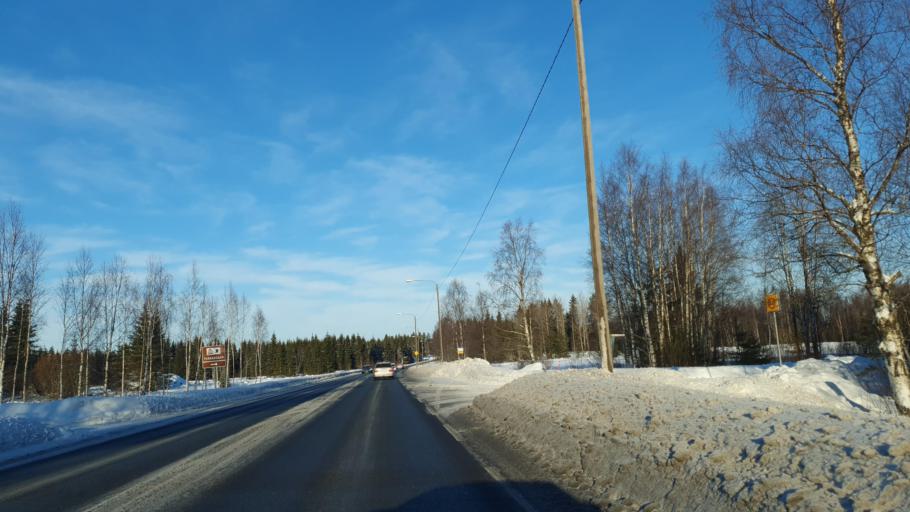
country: FI
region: Northern Ostrobothnia
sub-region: Oulu
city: Tyrnaevae
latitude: 64.9448
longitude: 25.6859
